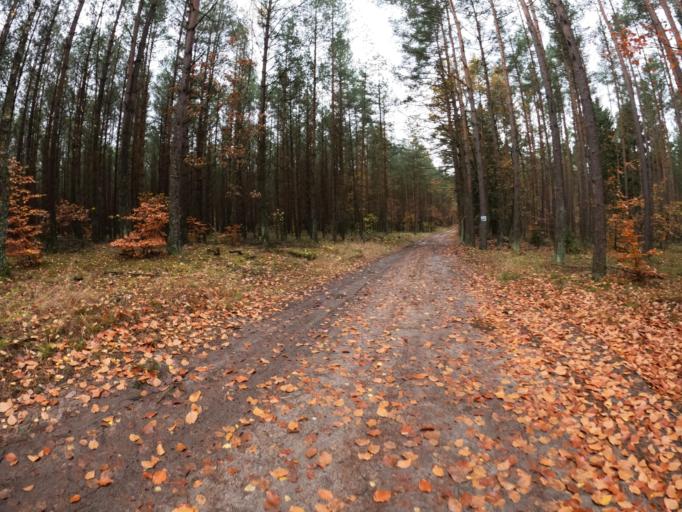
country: PL
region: West Pomeranian Voivodeship
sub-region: Powiat walecki
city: Tuczno
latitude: 53.2727
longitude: 16.2436
